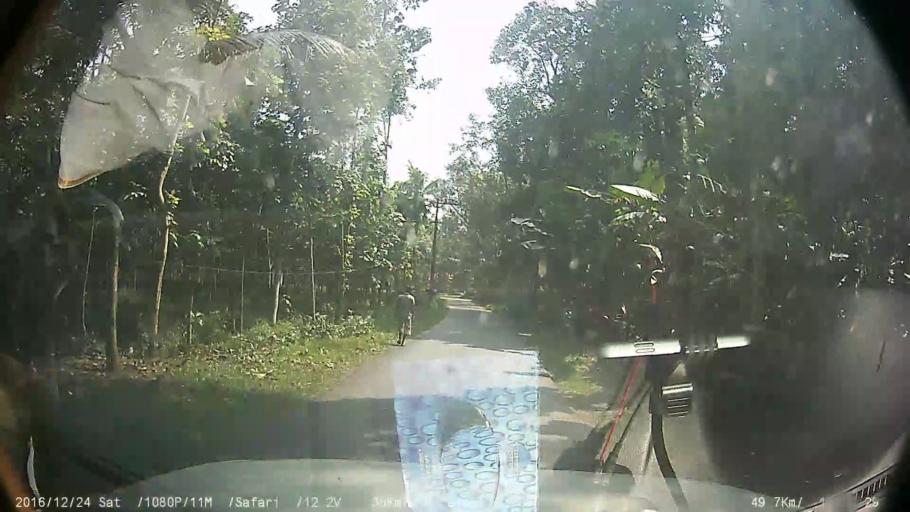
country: IN
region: Kerala
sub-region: Kottayam
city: Palackattumala
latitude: 9.8697
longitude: 76.6775
